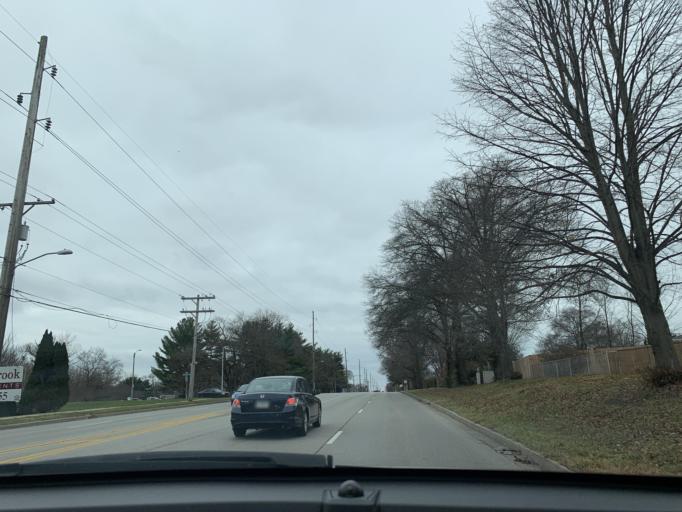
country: US
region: Illinois
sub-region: Sangamon County
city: Jerome
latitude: 39.7603
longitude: -89.6869
